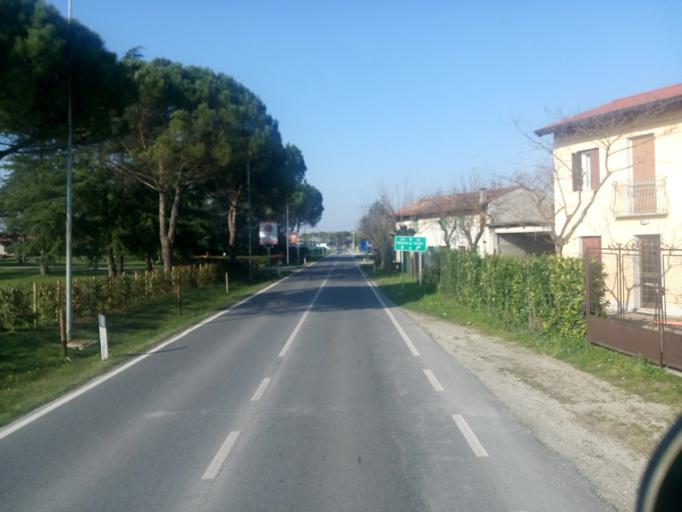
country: IT
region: Friuli Venezia Giulia
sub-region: Provincia di Udine
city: Castions di Strada
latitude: 45.9184
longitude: 13.1823
